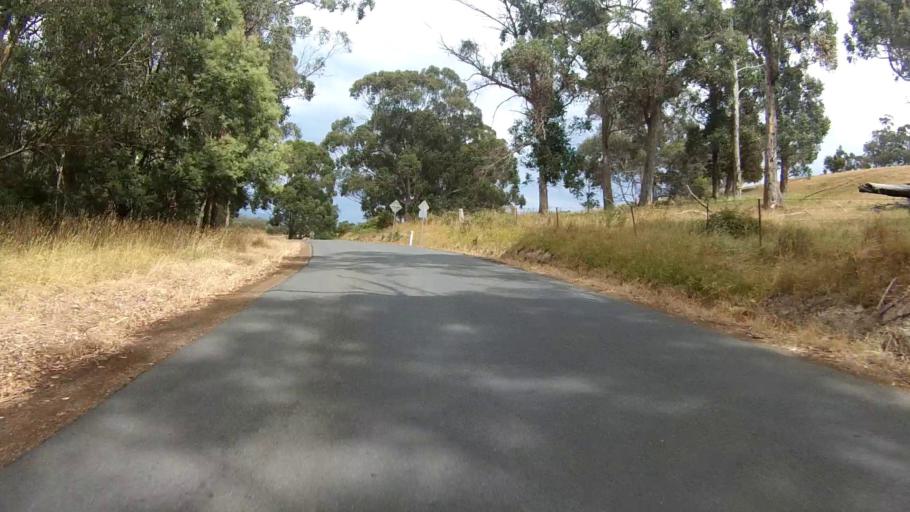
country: AU
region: Tasmania
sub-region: Huon Valley
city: Cygnet
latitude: -43.1812
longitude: 147.1133
